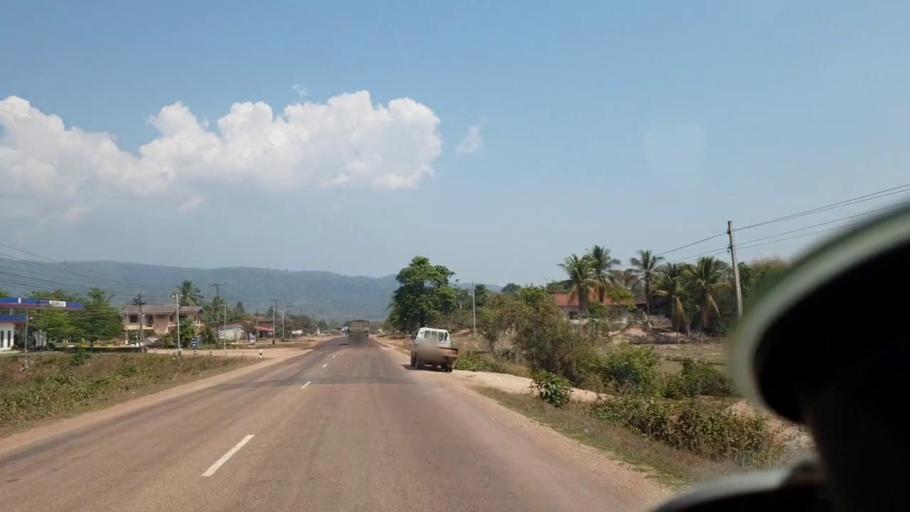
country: TH
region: Nong Khai
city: Rattanawapi
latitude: 18.1917
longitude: 103.0561
